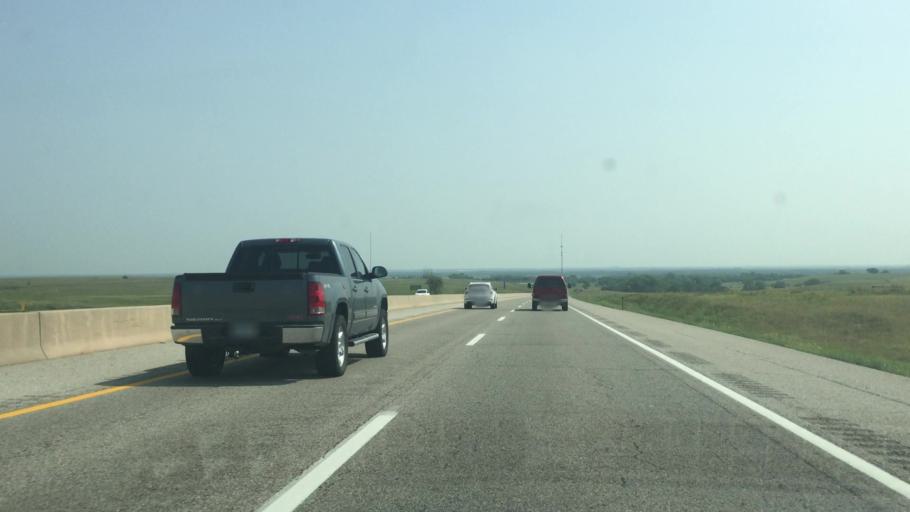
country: US
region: Kansas
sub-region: Lyon County
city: Emporia
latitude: 38.3253
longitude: -96.3157
